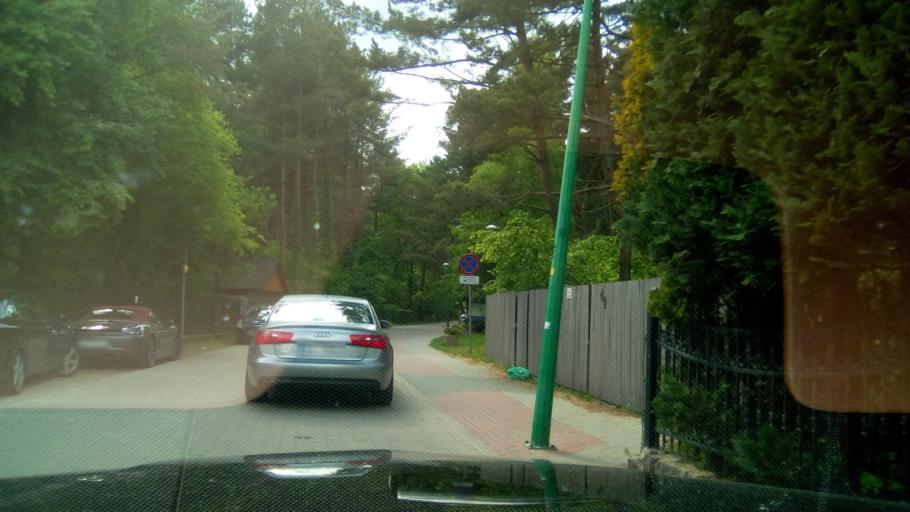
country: PL
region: Pomeranian Voivodeship
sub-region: Powiat pucki
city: Wierzchucino
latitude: 54.8296
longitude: 18.0810
